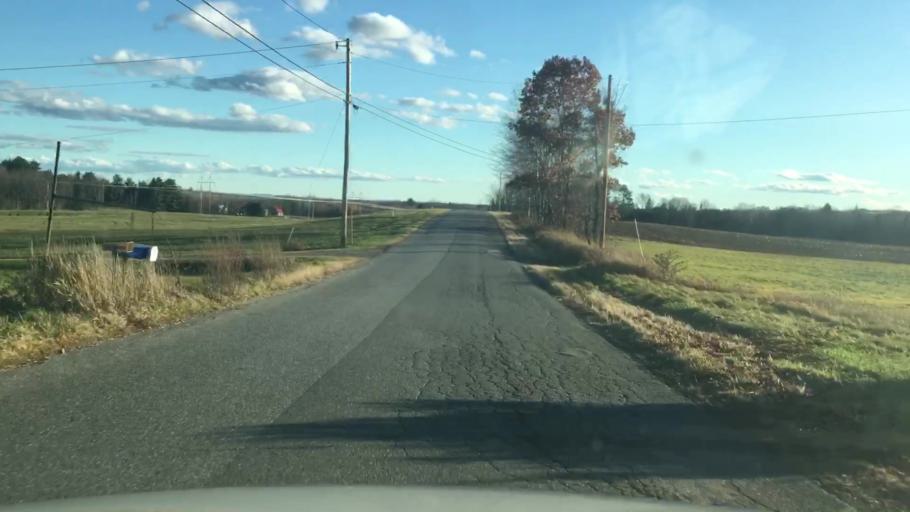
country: US
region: Maine
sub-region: Somerset County
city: Pittsfield
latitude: 44.7895
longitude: -69.4101
